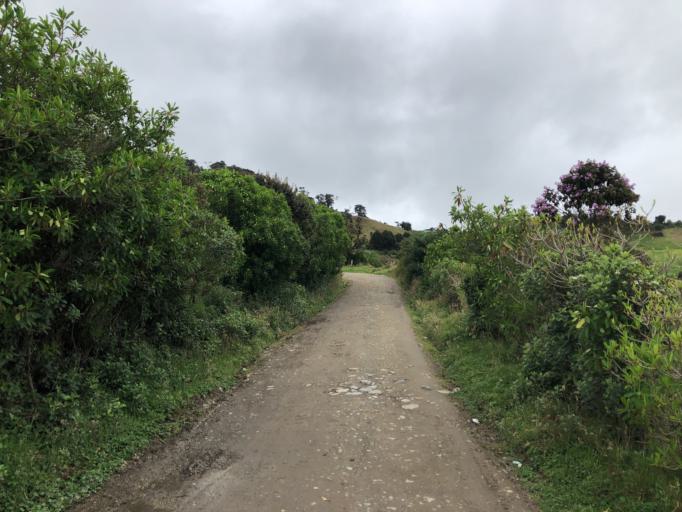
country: CO
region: Cauca
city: Totoro
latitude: 2.4975
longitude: -76.3492
